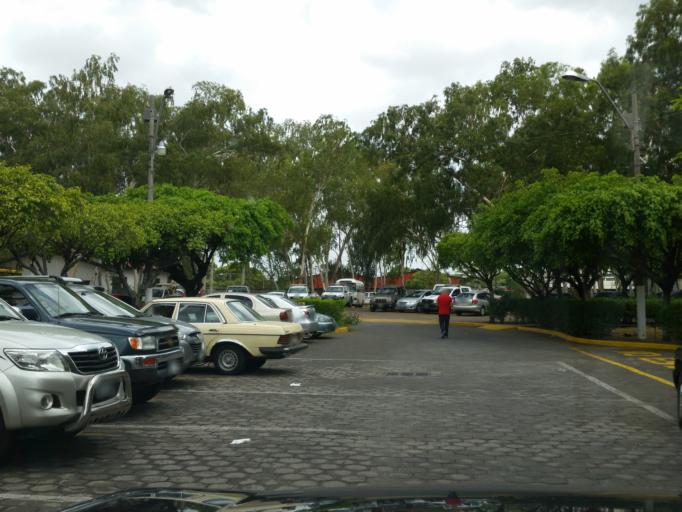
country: NI
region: Managua
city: Managua
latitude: 12.1479
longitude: -86.2507
